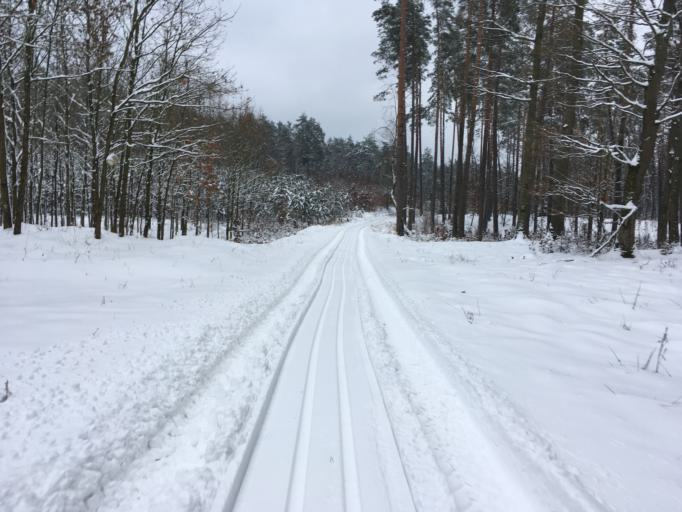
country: PL
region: Kujawsko-Pomorskie
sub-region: Powiat brodnicki
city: Gorzno
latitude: 53.1953
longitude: 19.6764
